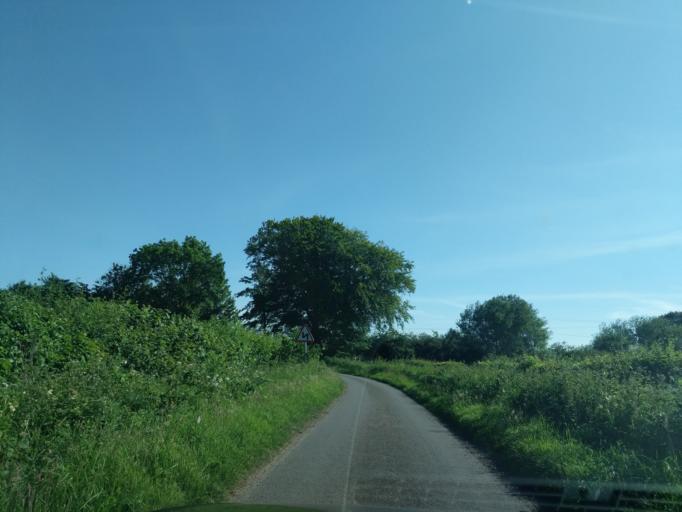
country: GB
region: Scotland
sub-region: East Lothian
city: Ormiston
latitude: 55.8794
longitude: -2.9339
